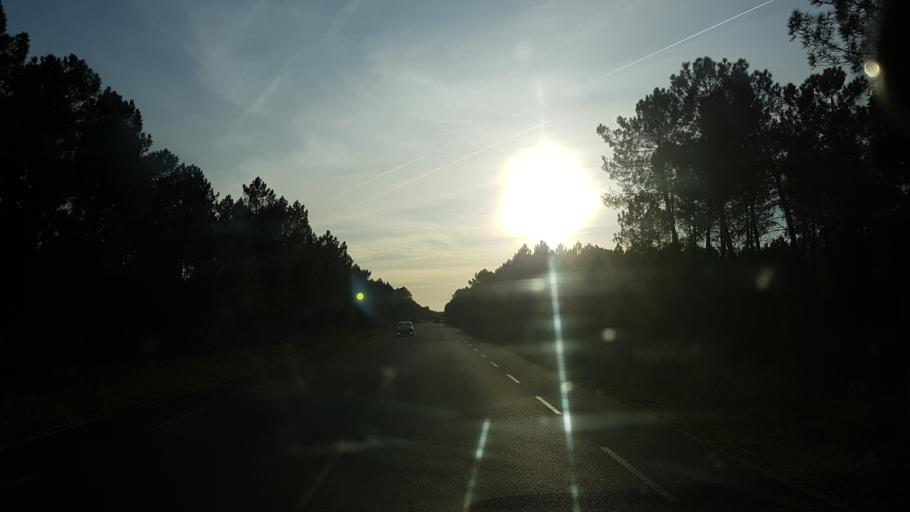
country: FR
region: Aquitaine
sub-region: Departement de la Gironde
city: Martignas-sur-Jalle
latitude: 44.8379
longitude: -0.7565
